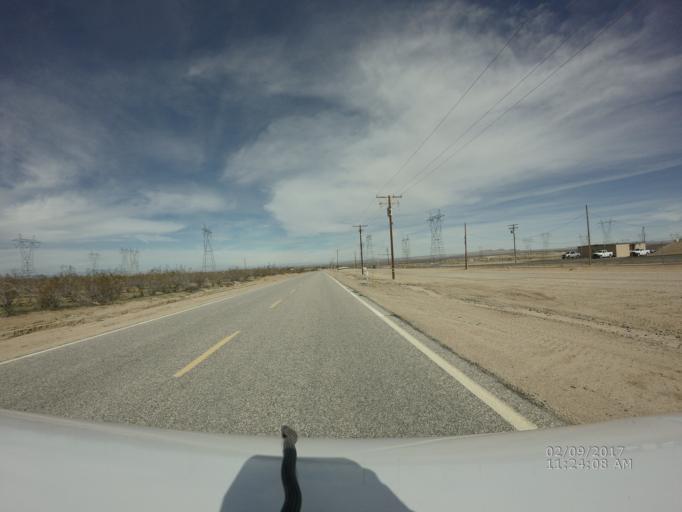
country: US
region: California
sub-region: Los Angeles County
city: Littlerock
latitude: 34.5124
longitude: -117.9231
